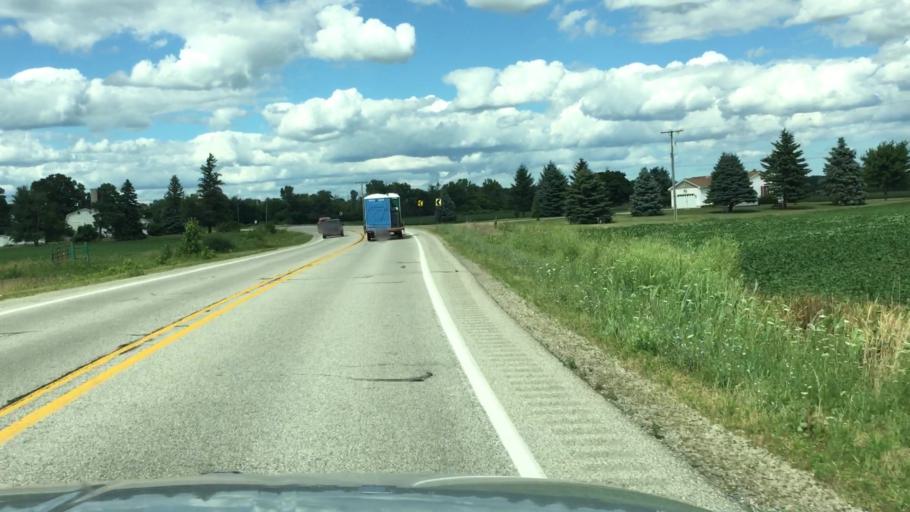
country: US
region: Michigan
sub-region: Saint Clair County
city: Capac
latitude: 42.9451
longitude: -82.9452
